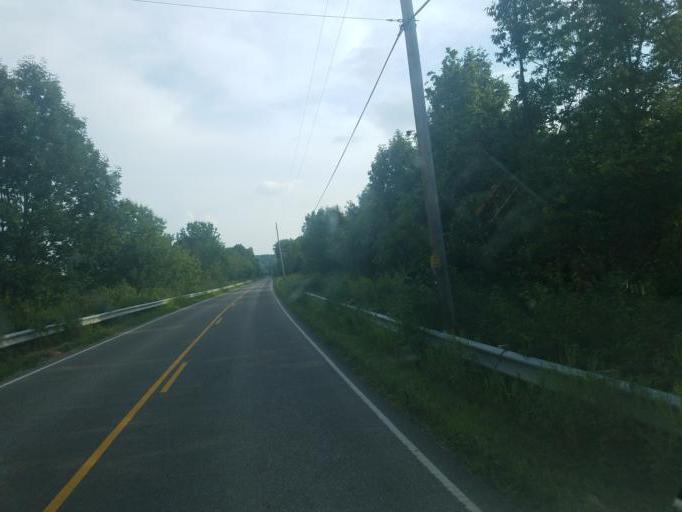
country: US
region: Ohio
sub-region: Knox County
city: Fredericktown
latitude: 40.5182
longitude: -82.5909
